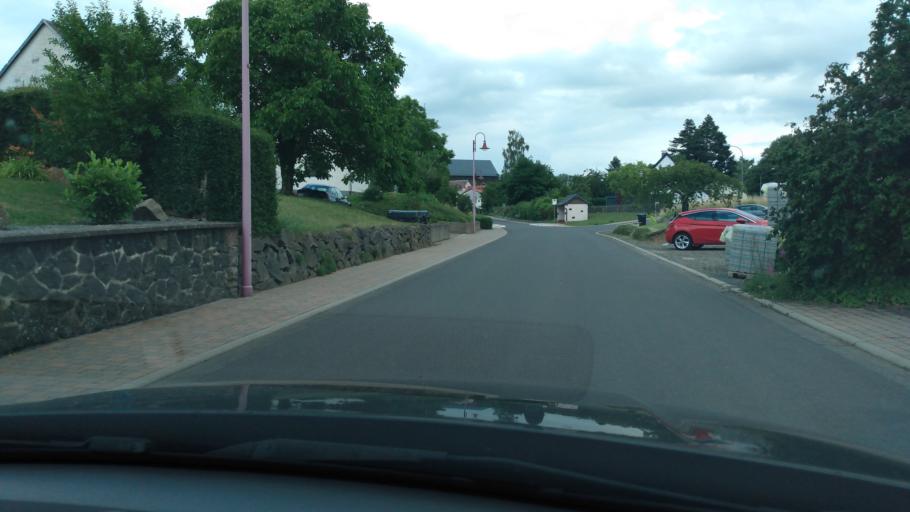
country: DE
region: Rheinland-Pfalz
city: Udersdorf
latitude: 50.1505
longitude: 6.8023
